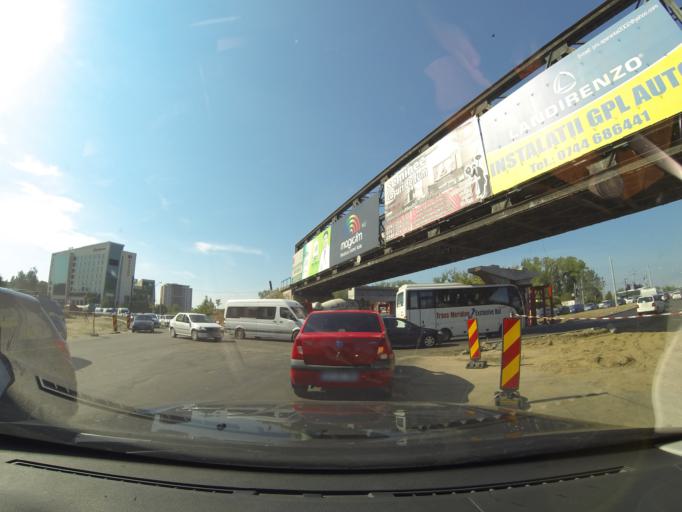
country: RO
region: Arges
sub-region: Comuna Albestii de Arges
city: Pitesti
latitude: 44.8645
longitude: 24.8797
